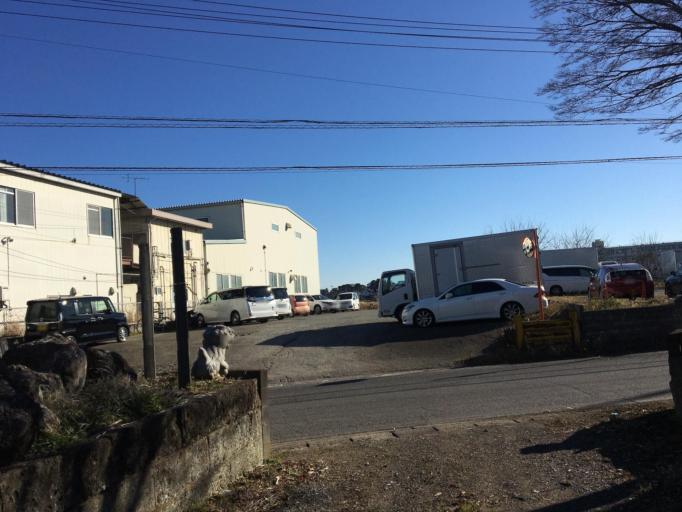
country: JP
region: Saitama
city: Ageoshimo
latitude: 35.9745
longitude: 139.6313
